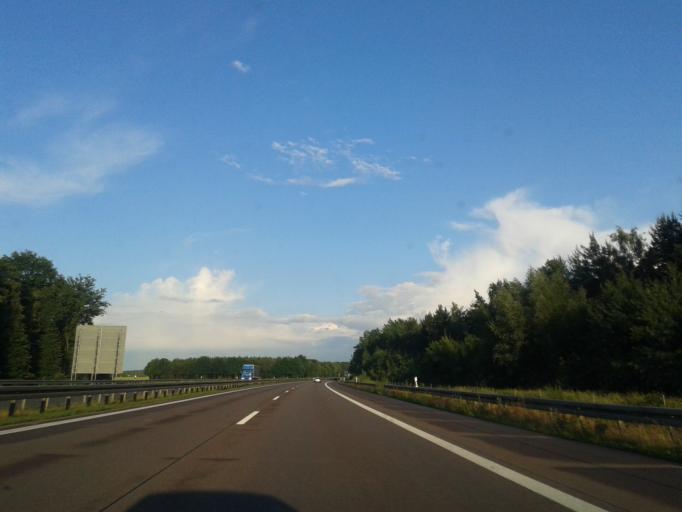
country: DE
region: Saxony
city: Naunhof
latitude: 51.3026
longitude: 12.6060
